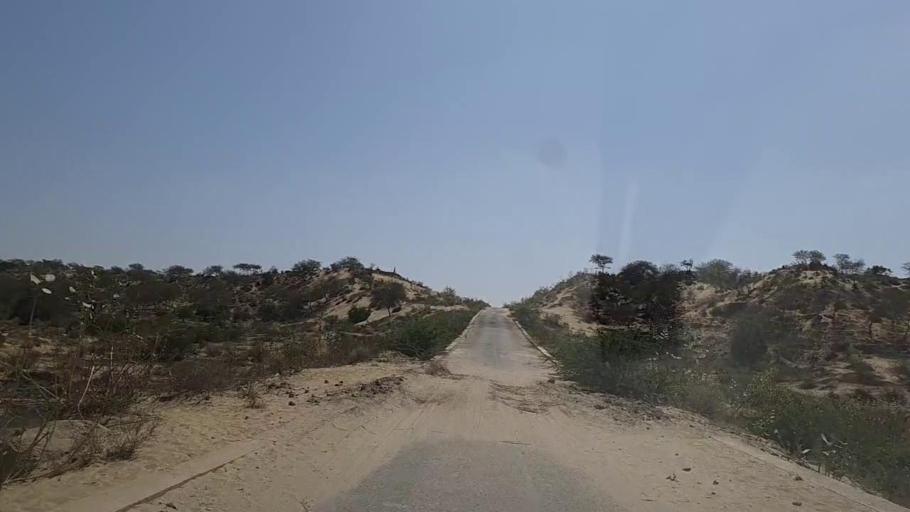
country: PK
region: Sindh
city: Diplo
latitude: 24.5071
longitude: 69.4238
